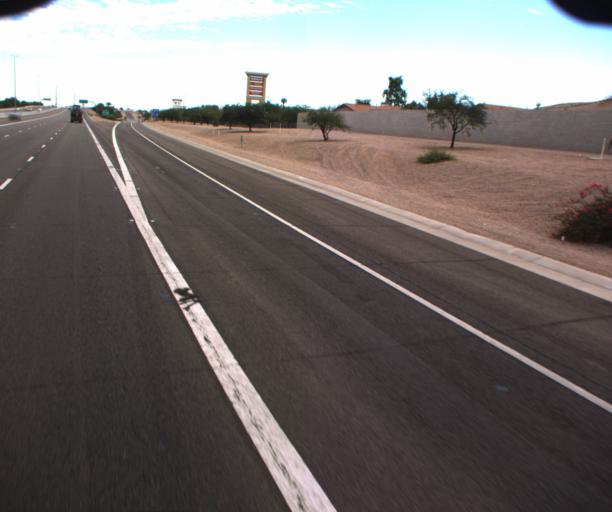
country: US
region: Arizona
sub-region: Maricopa County
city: Chandler
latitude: 33.2871
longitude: -111.8472
